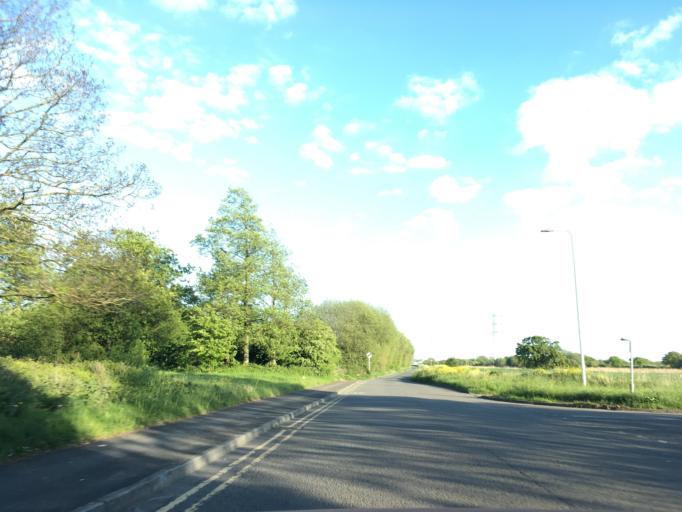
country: GB
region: Wales
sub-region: Newport
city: Marshfield
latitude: 51.5280
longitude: -3.0810
